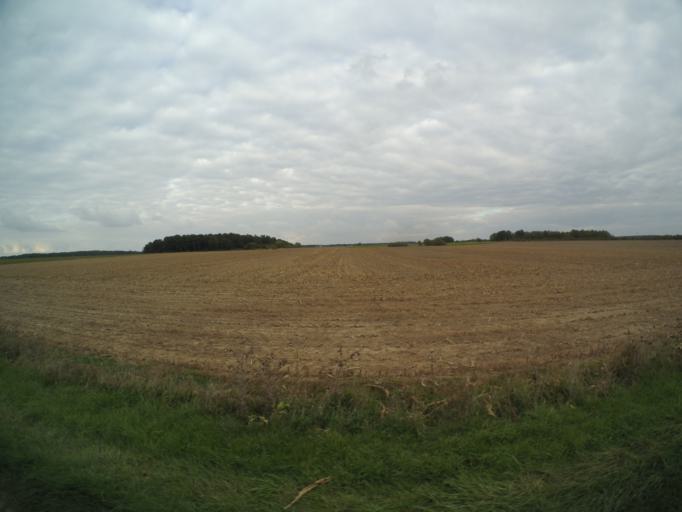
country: FR
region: Centre
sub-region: Departement d'Indre-et-Loire
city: Auzouer-en-Touraine
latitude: 47.4989
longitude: 0.9619
